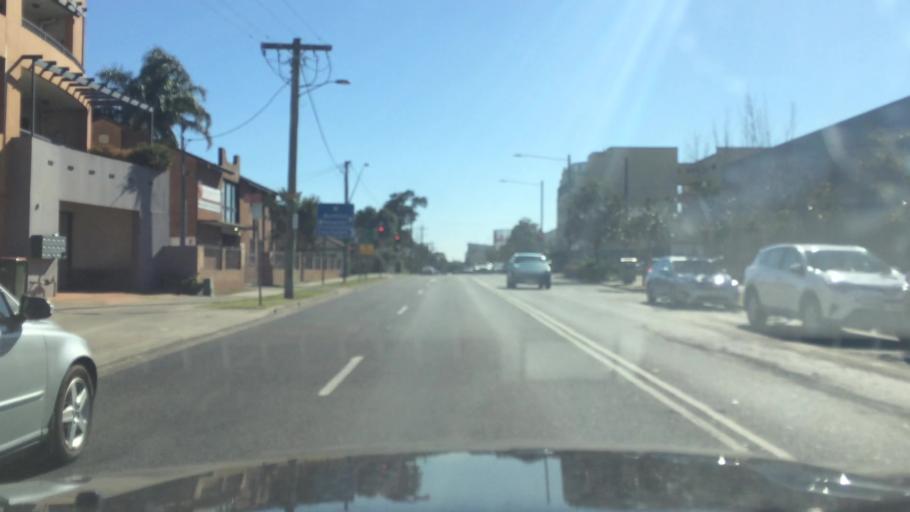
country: AU
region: New South Wales
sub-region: Fairfield
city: Liverpool
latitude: -33.9229
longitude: 150.9212
